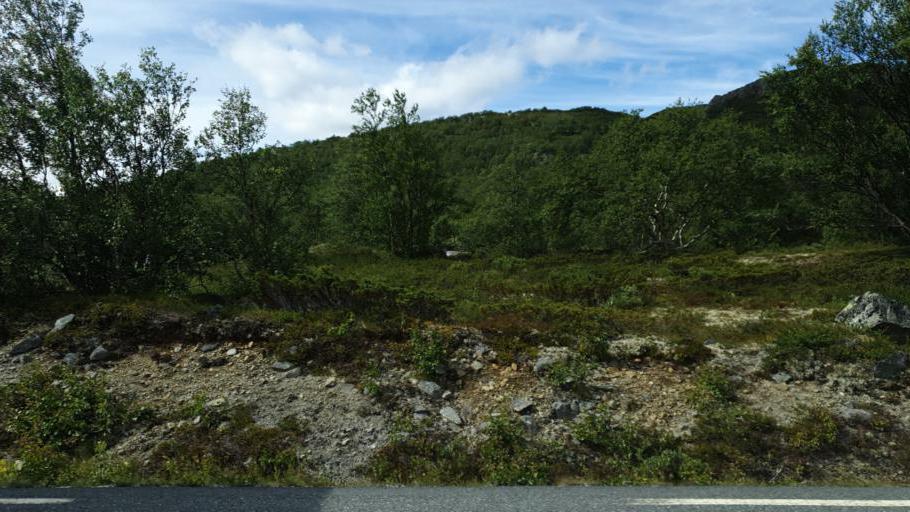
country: NO
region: Oppland
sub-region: Oystre Slidre
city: Heggenes
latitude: 61.4983
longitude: 8.8442
